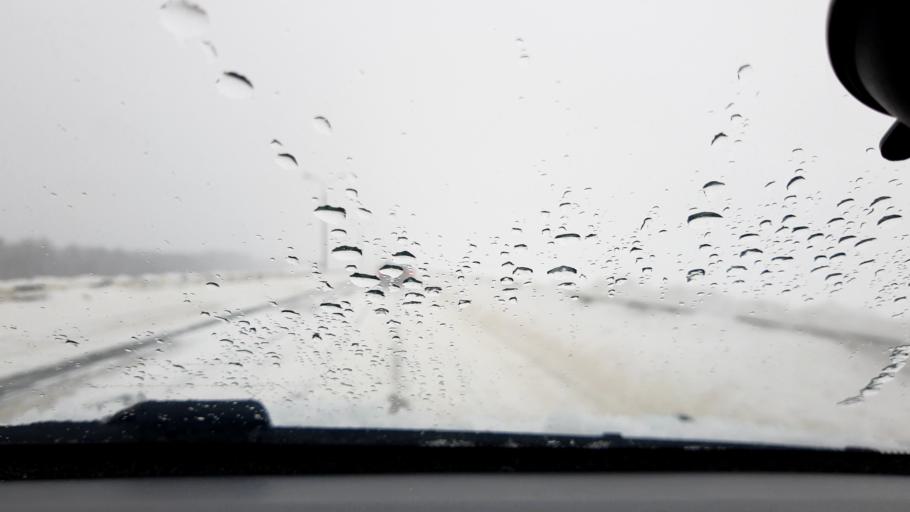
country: RU
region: Nizjnij Novgorod
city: Pervomayskiy
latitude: 56.6410
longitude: 43.2937
